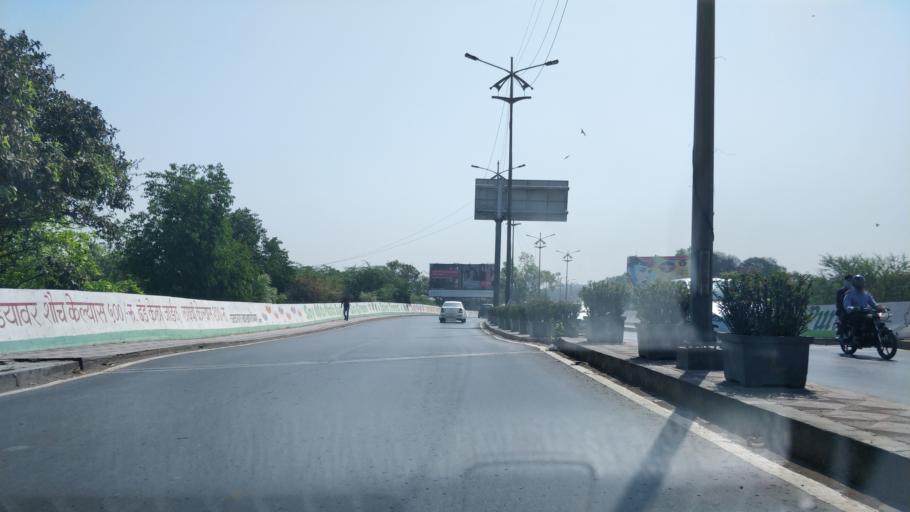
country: IN
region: Maharashtra
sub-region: Pune Division
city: Shivaji Nagar
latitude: 18.5329
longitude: 73.8570
